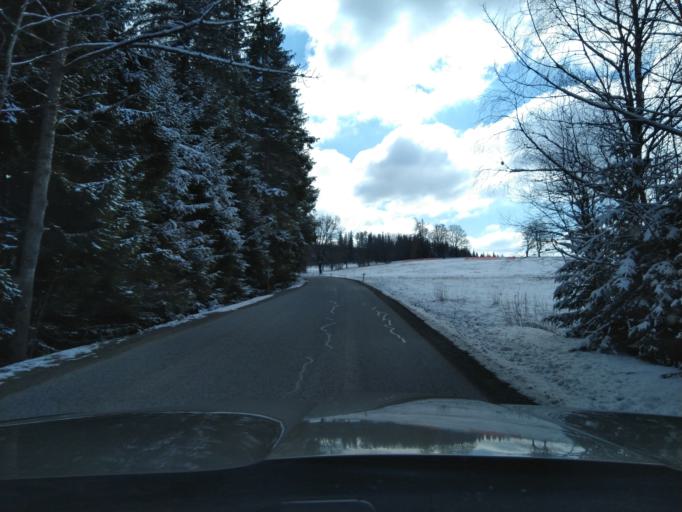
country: CZ
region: Jihocesky
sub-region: Okres Prachatice
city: Zdikov
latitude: 49.0473
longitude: 13.6696
